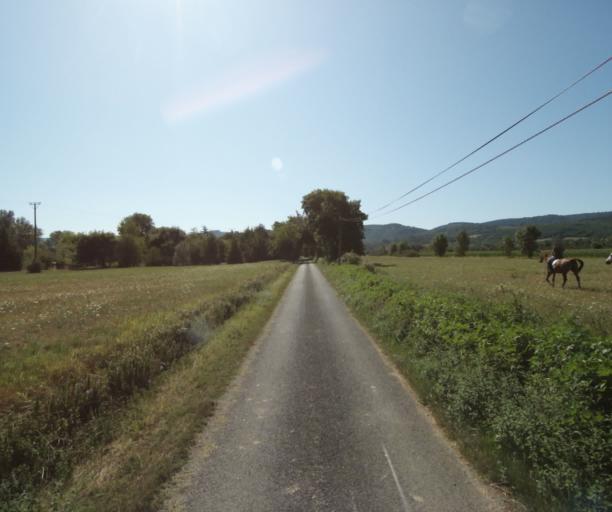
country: FR
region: Midi-Pyrenees
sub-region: Departement de la Haute-Garonne
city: Revel
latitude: 43.4598
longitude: 2.0291
